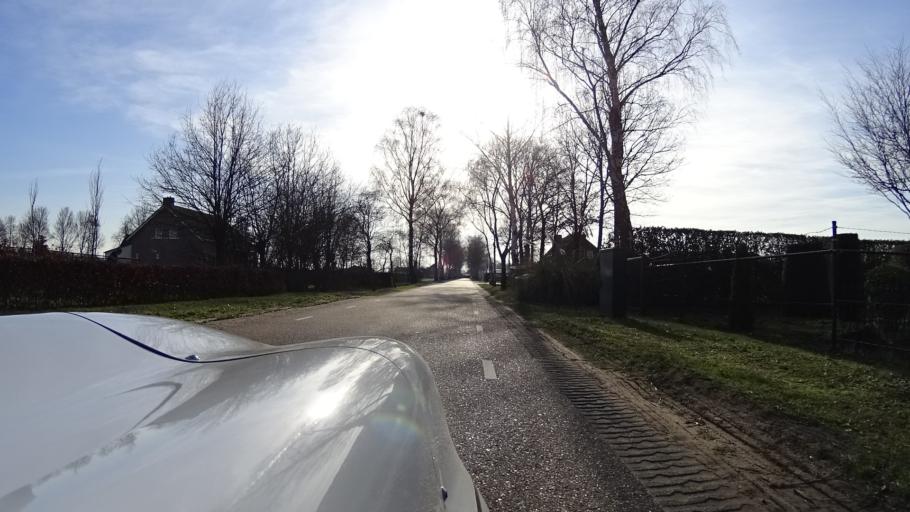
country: NL
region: North Brabant
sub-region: Gemeente Boekel
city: Boekel
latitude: 51.5687
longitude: 5.6442
